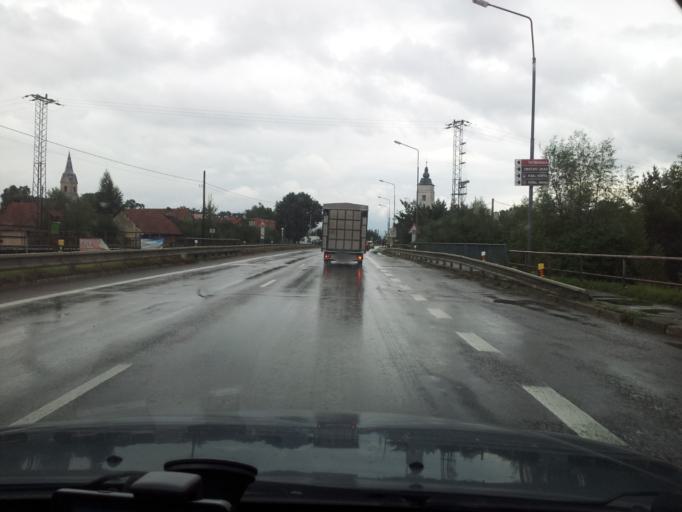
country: SK
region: Presovsky
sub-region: Okres Poprad
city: Poprad
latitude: 49.1102
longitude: 20.3577
